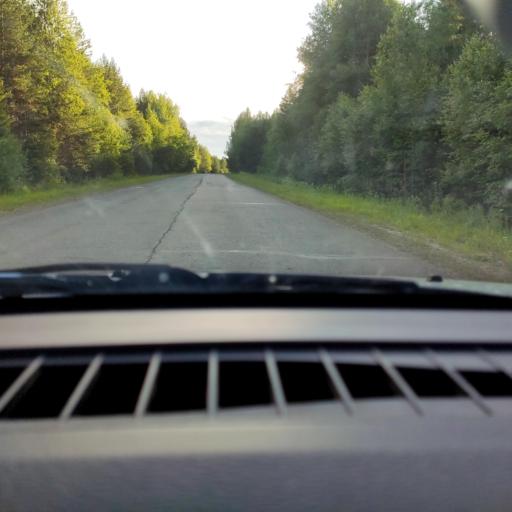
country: RU
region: Perm
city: Uinskoye
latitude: 57.0827
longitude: 56.6173
